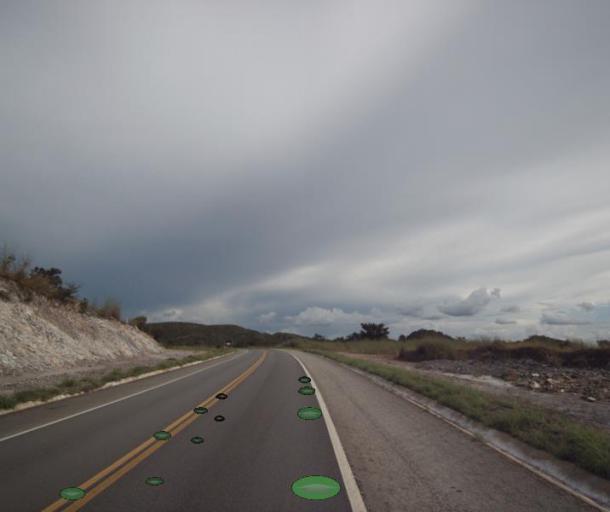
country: BR
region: Goias
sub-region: Barro Alto
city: Barro Alto
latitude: -15.1036
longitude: -48.7499
